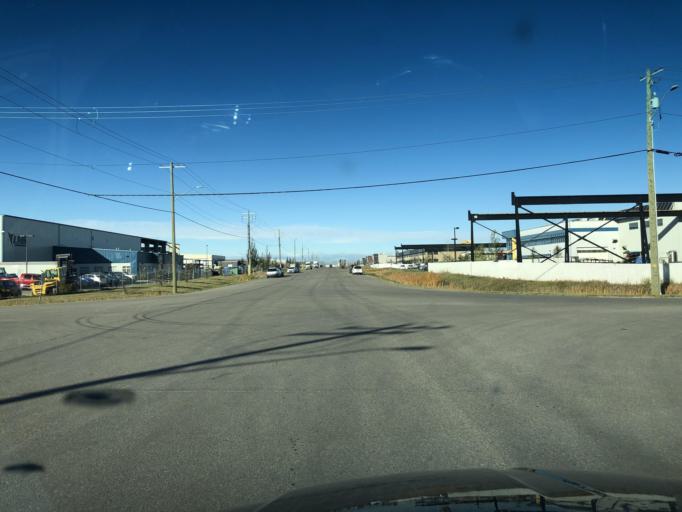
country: CA
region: Alberta
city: Chestermere
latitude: 50.9625
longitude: -113.8968
